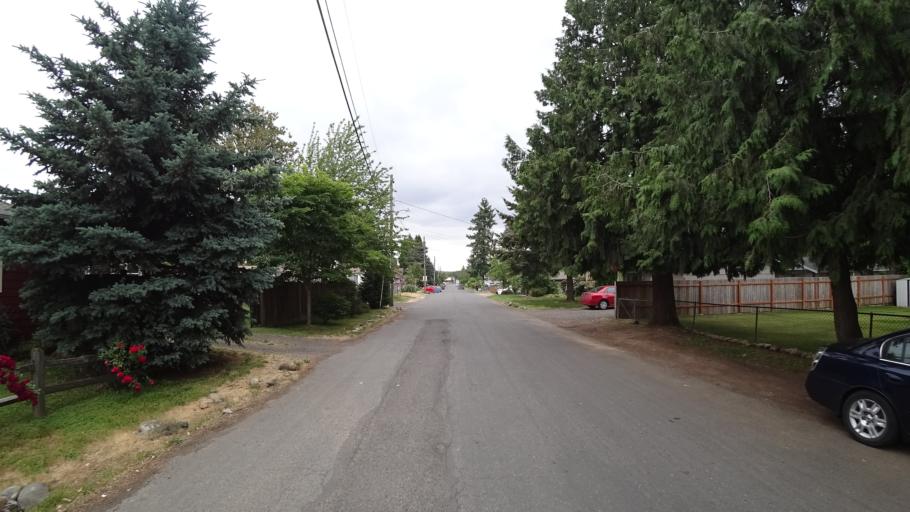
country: US
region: Oregon
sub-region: Multnomah County
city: Lents
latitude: 45.4720
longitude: -122.5829
